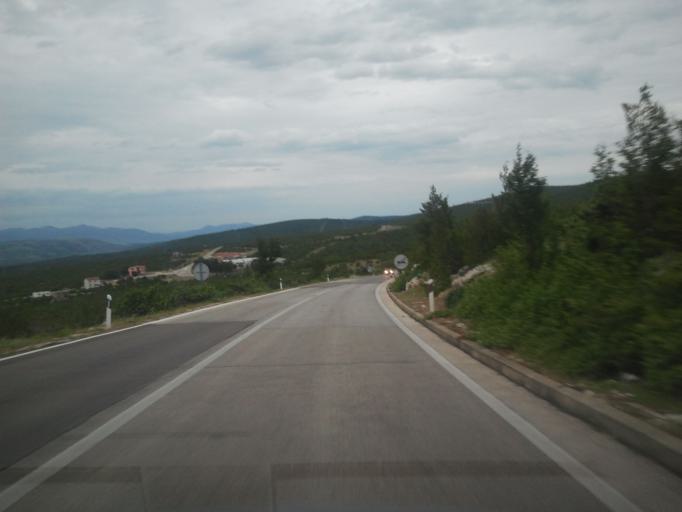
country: HR
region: Zadarska
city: Obrovac
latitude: 44.1954
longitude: 15.6733
